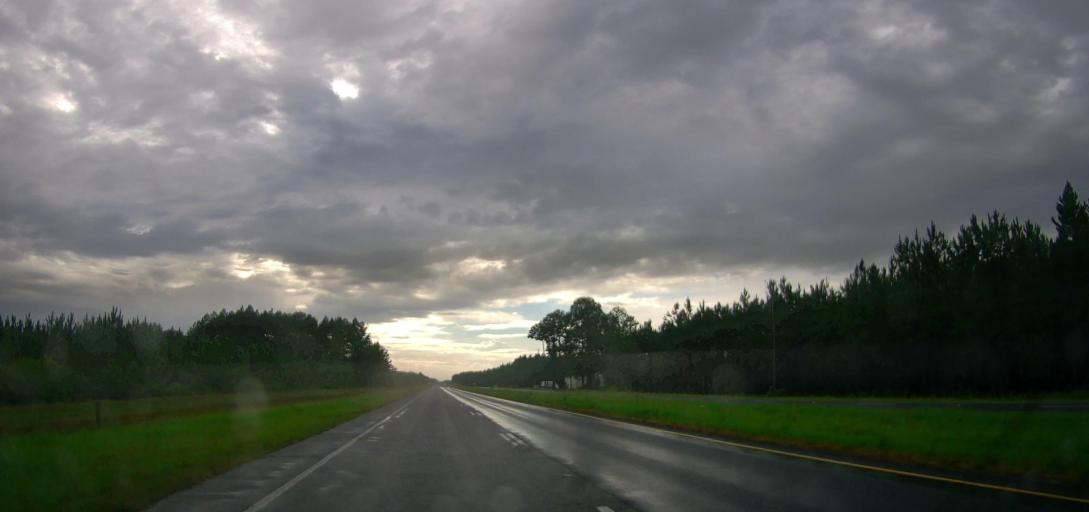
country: US
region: Georgia
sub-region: Ware County
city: Deenwood
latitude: 31.2569
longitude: -82.4939
